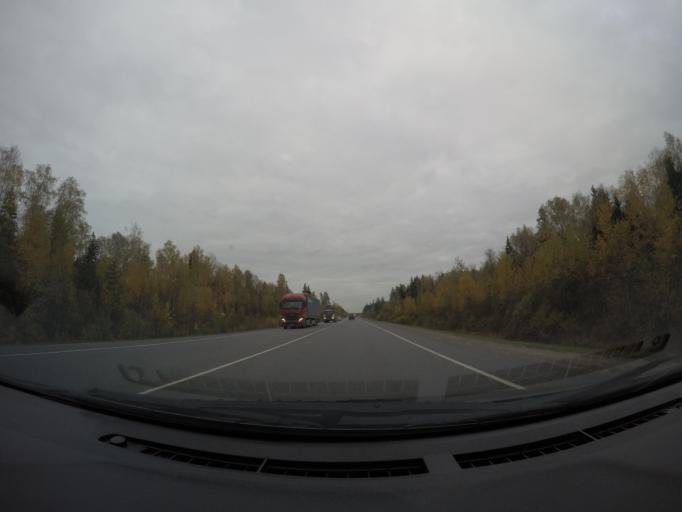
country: RU
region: Moskovskaya
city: Fryazevo
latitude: 55.7106
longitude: 38.4273
